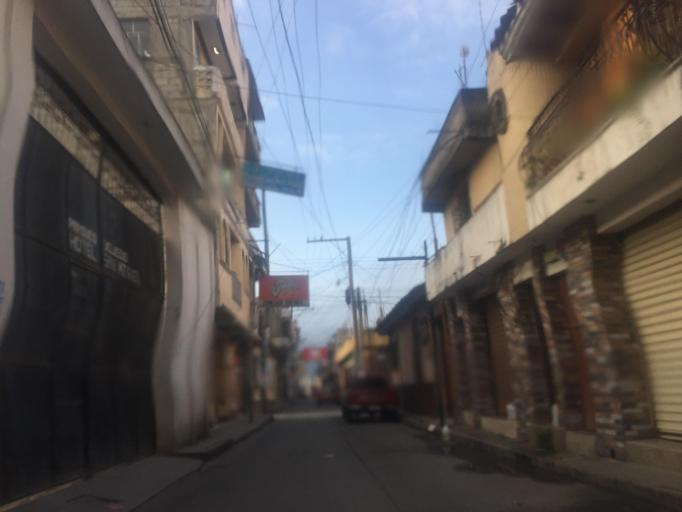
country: GT
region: Totonicapan
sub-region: Municipio de Totonicapan
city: Totonicapan
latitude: 14.9132
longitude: -91.3610
